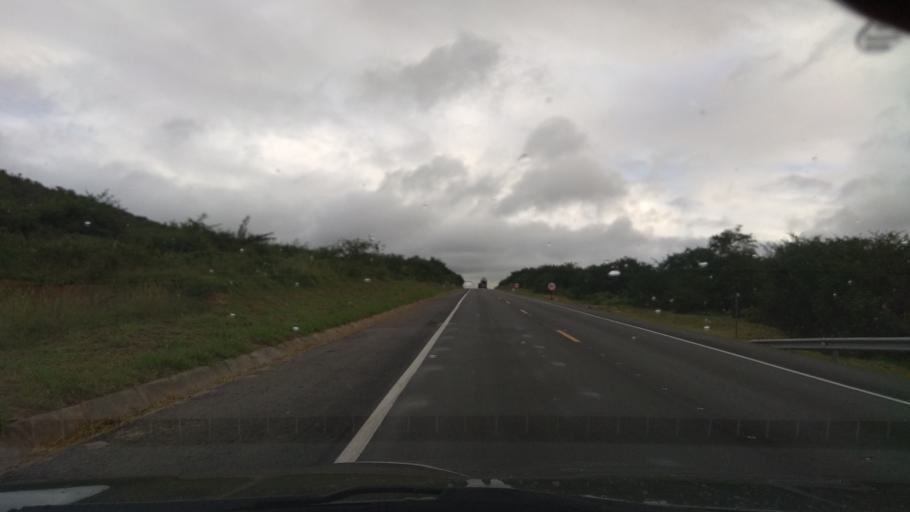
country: BR
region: Bahia
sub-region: Santa Ines
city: Santa Ines
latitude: -13.2823
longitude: -40.0183
